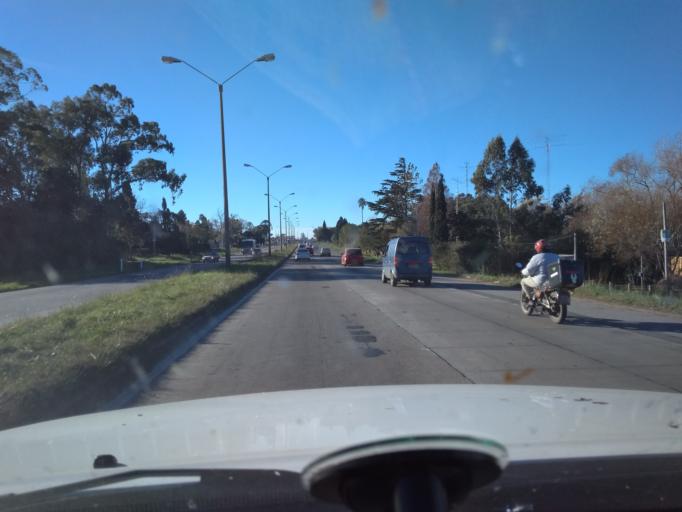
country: UY
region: Canelones
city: Colonia Nicolich
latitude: -34.7853
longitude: -56.0620
